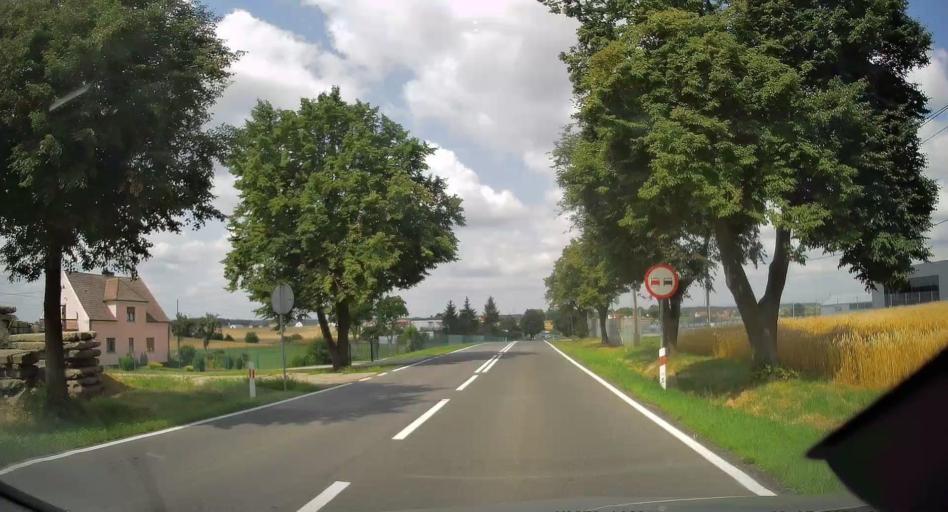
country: PL
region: Opole Voivodeship
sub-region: Powiat kedzierzynsko-kozielski
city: Wiekszyce
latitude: 50.3337
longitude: 18.0781
